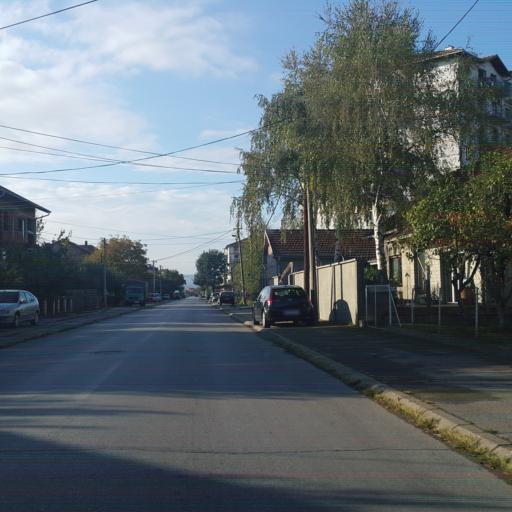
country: RS
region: Central Serbia
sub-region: Rasinski Okrug
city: Krusevac
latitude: 43.5710
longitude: 21.3489
